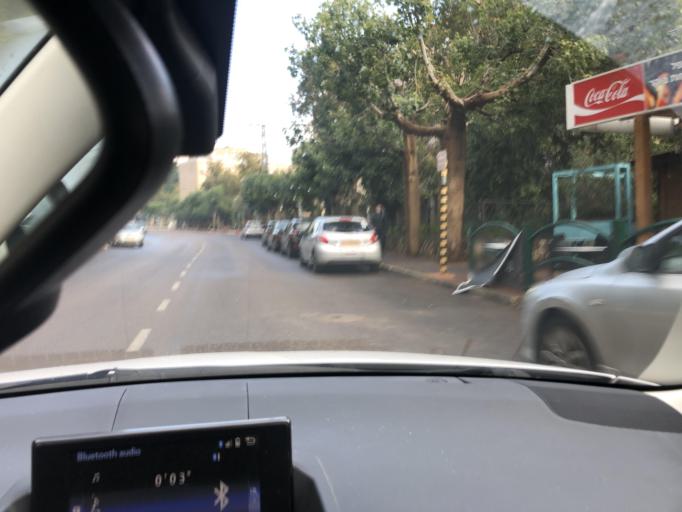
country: IL
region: Central District
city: Ganne Tiqwa
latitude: 32.0594
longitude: 34.8694
